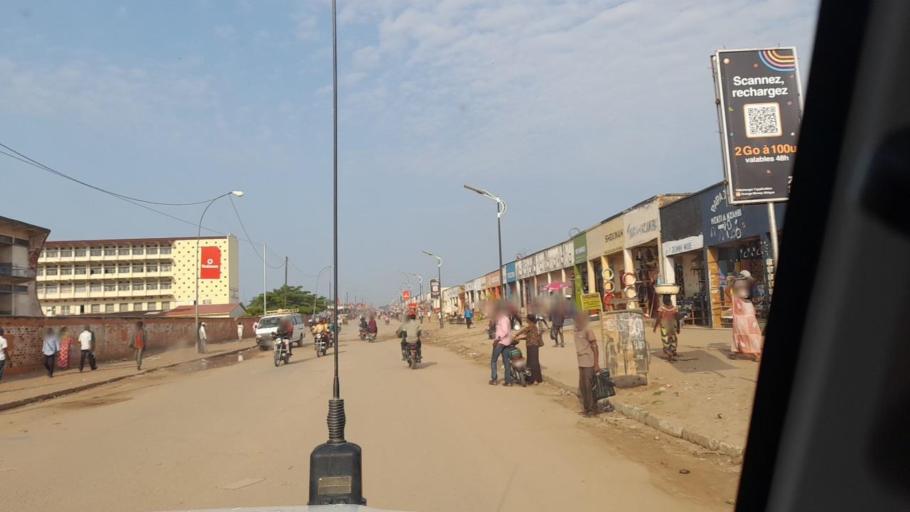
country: CD
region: Kasai-Occidental
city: Kananga
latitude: -5.8942
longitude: 22.4023
